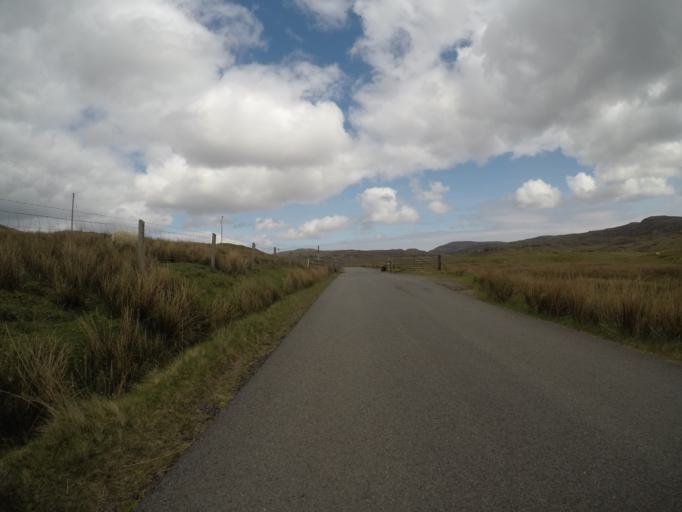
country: GB
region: Scotland
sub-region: Highland
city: Isle of Skye
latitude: 57.3674
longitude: -6.3869
